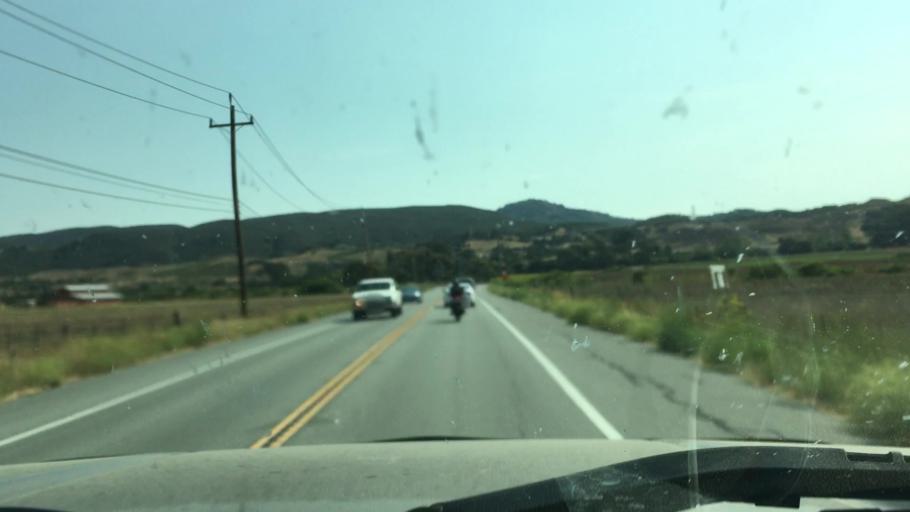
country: US
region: California
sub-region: San Luis Obispo County
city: San Luis Obispo
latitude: 35.2787
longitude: -120.7107
